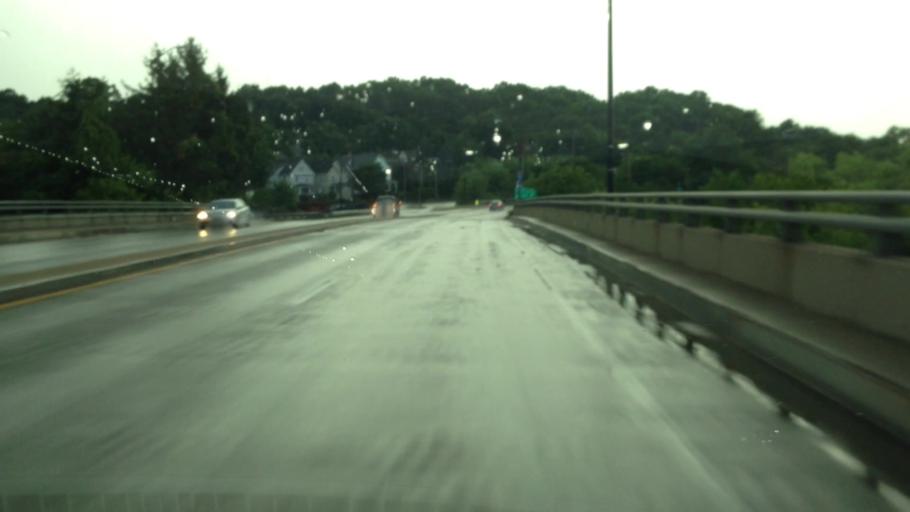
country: US
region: Ohio
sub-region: Summit County
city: Portage Lakes
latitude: 41.0427
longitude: -81.5467
